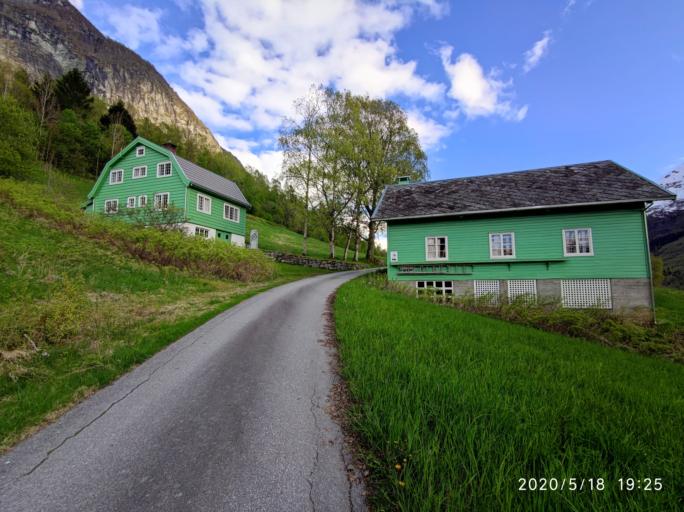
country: NO
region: Sogn og Fjordane
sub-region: Stryn
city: Stryn
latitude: 61.8332
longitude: 6.8141
